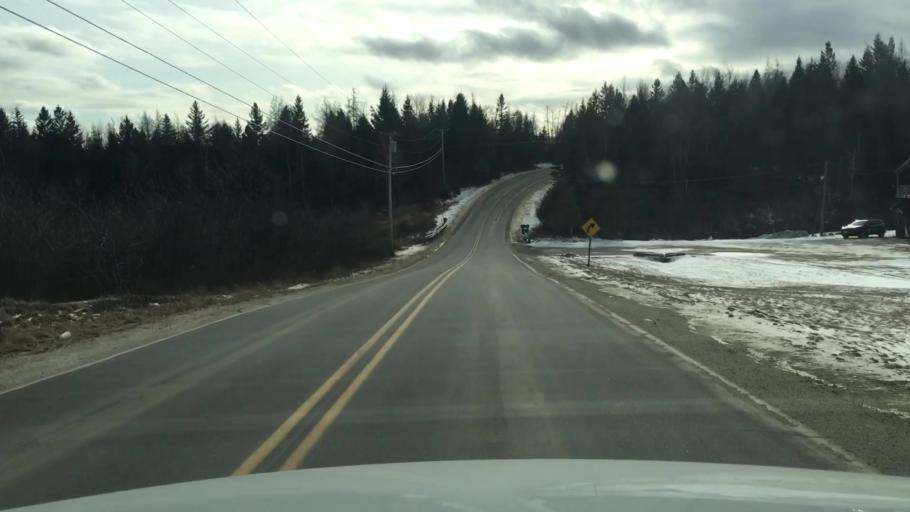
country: US
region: Maine
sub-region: Washington County
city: Jonesport
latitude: 44.6292
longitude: -67.5964
